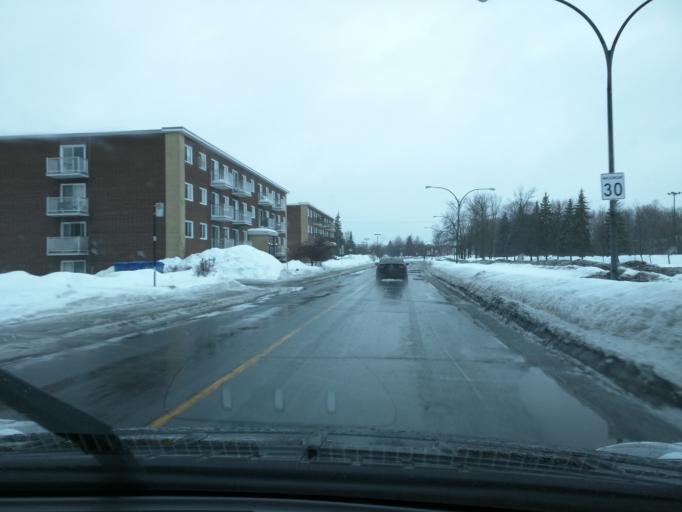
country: CA
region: Quebec
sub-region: Monteregie
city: Longueuil
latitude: 45.5423
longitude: -73.4724
